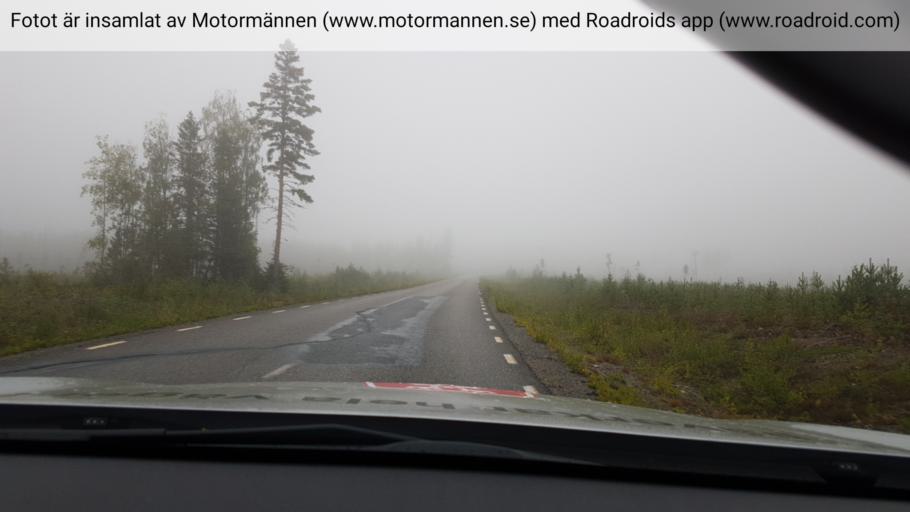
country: SE
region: Vaesterbotten
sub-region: Umea Kommun
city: Ersmark
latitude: 64.1866
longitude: 20.3346
